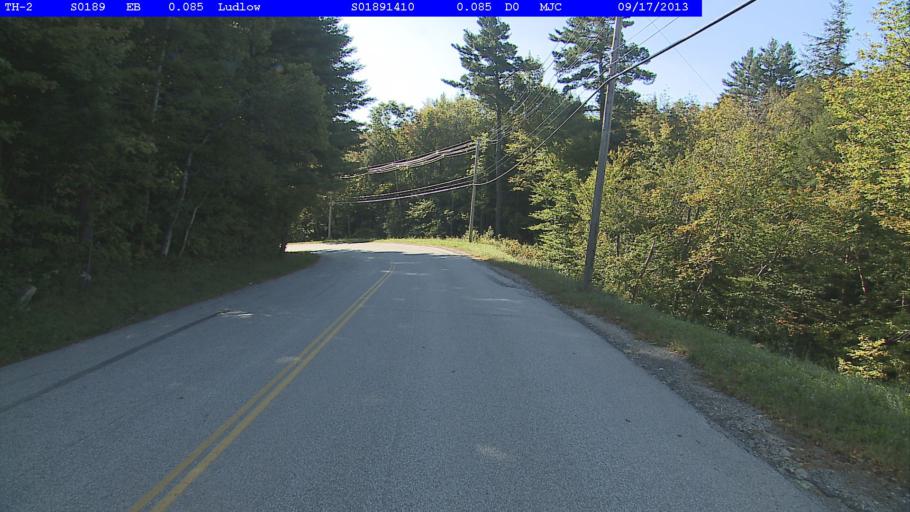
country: US
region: Vermont
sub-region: Windsor County
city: Chester
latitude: 43.3998
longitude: -72.7150
